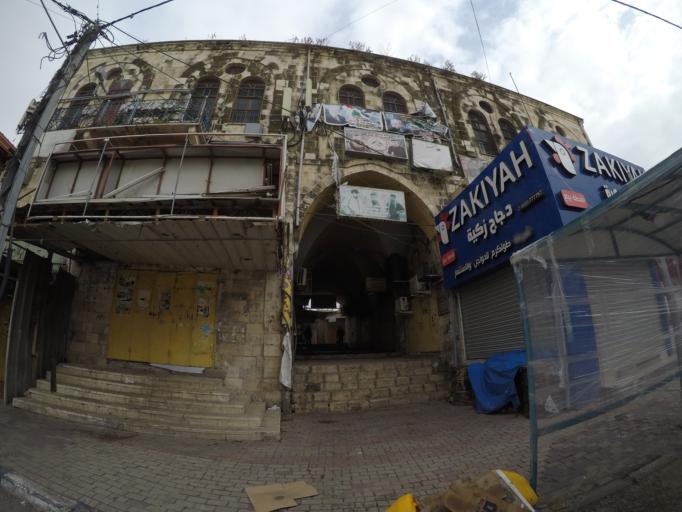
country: PS
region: West Bank
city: Janin
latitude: 32.4600
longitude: 35.3018
